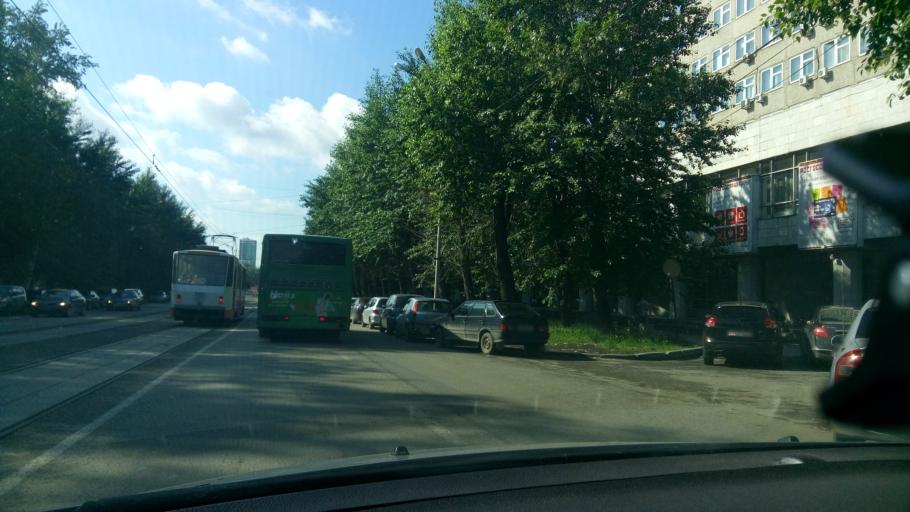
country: RU
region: Sverdlovsk
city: Yekaterinburg
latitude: 56.8451
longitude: 60.6446
